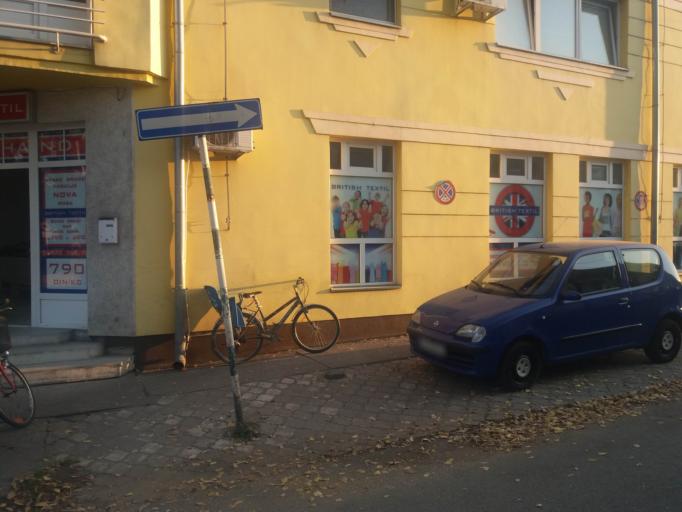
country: RS
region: Autonomna Pokrajina Vojvodina
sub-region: Severnobacki Okrug
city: Subotica
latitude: 46.0992
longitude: 19.6541
